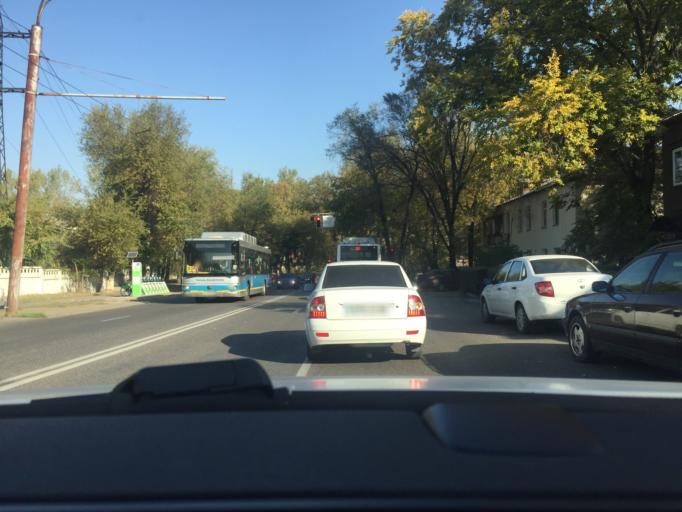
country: KZ
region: Almaty Qalasy
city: Almaty
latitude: 43.2447
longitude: 76.9080
